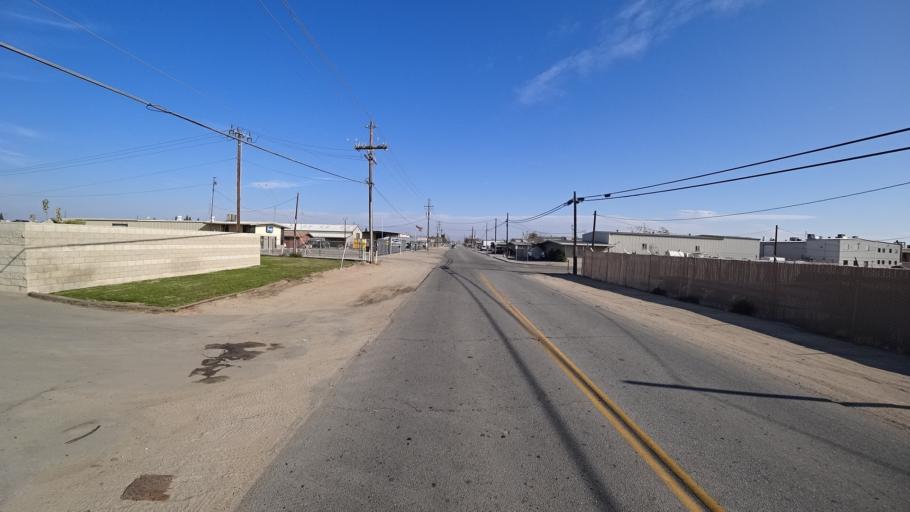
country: US
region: California
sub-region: Kern County
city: Greenacres
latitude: 35.3905
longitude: -119.0836
